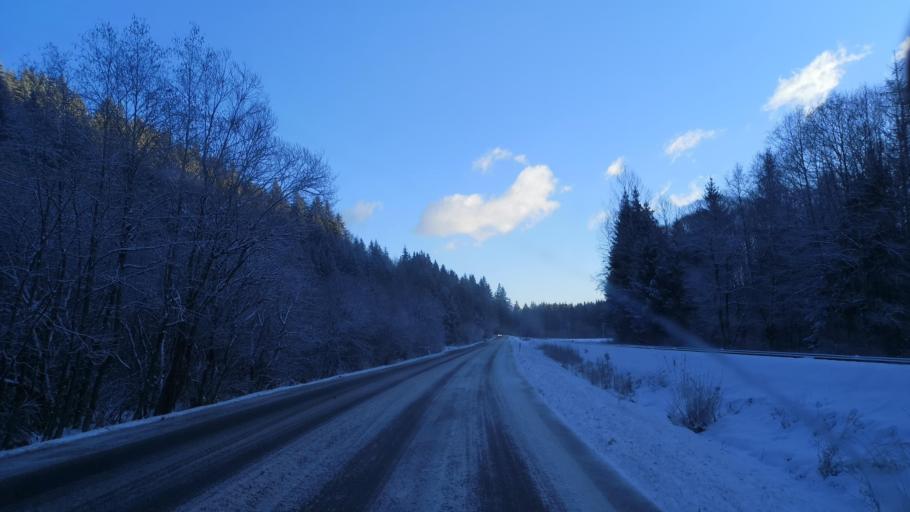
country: SK
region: Banskobystricky
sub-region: Okres Banska Bystrica
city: Brezno
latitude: 48.8346
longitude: 19.7822
